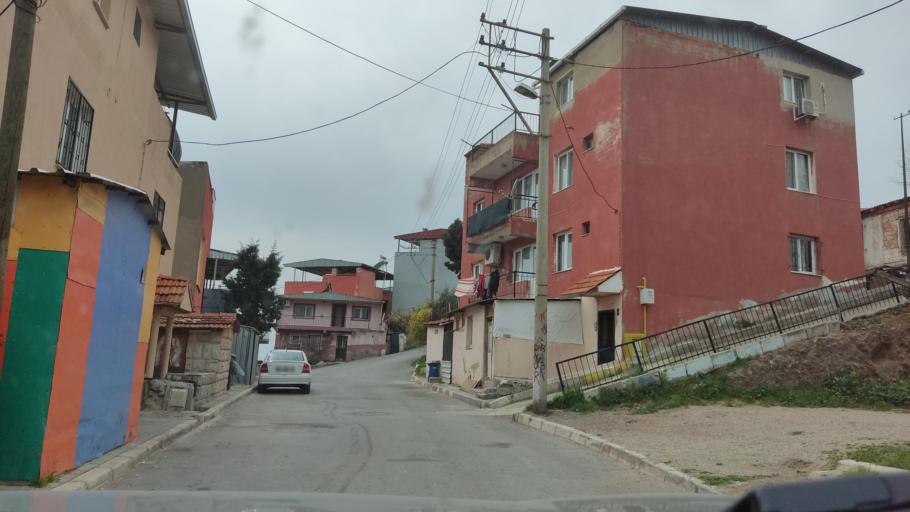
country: TR
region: Izmir
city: Karsiyaka
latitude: 38.4986
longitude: 27.0758
